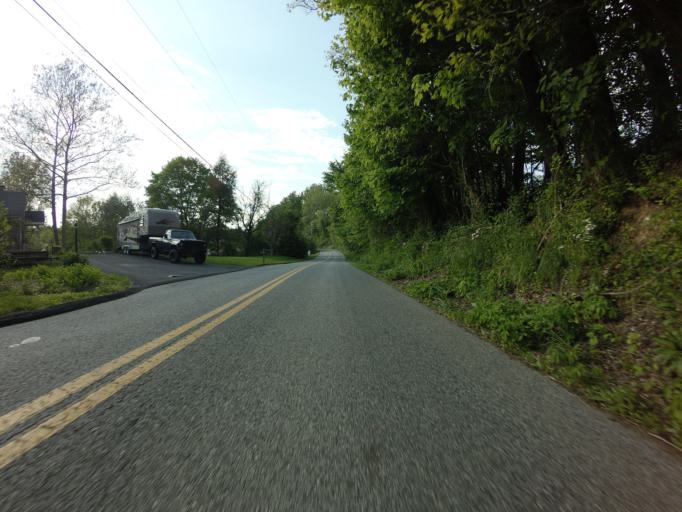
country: US
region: Maryland
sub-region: Baltimore County
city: Hunt Valley
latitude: 39.5195
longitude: -76.7098
